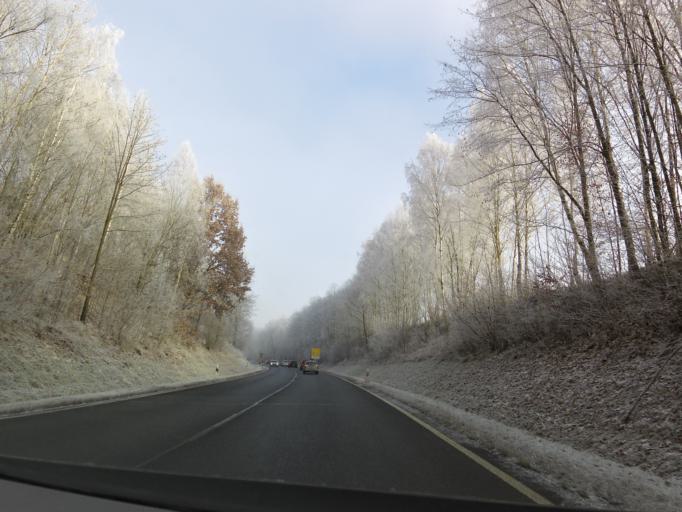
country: DE
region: Bavaria
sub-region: Upper Franconia
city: Arzberg
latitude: 50.0617
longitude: 12.1813
